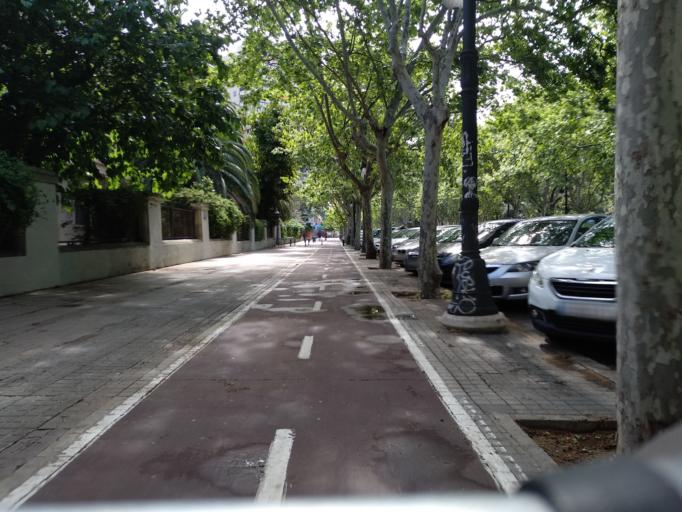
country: ES
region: Valencia
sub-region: Provincia de Valencia
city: Valencia
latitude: 39.4778
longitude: -0.3595
